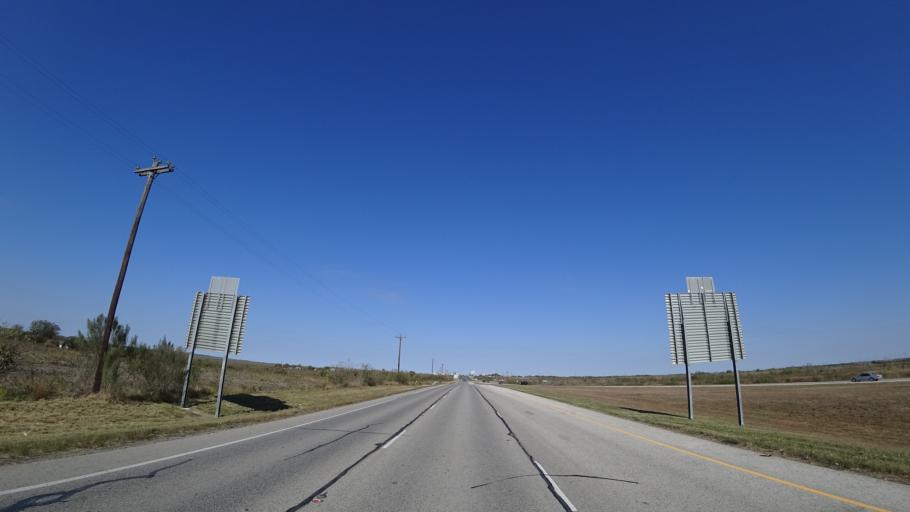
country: US
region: Texas
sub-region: Travis County
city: Onion Creek
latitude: 30.0859
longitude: -97.6935
